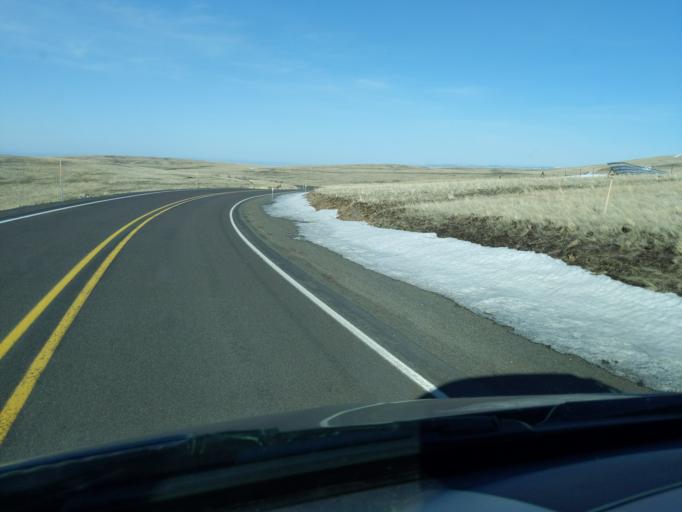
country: US
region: Oregon
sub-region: Umatilla County
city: Pilot Rock
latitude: 45.3035
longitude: -119.0048
